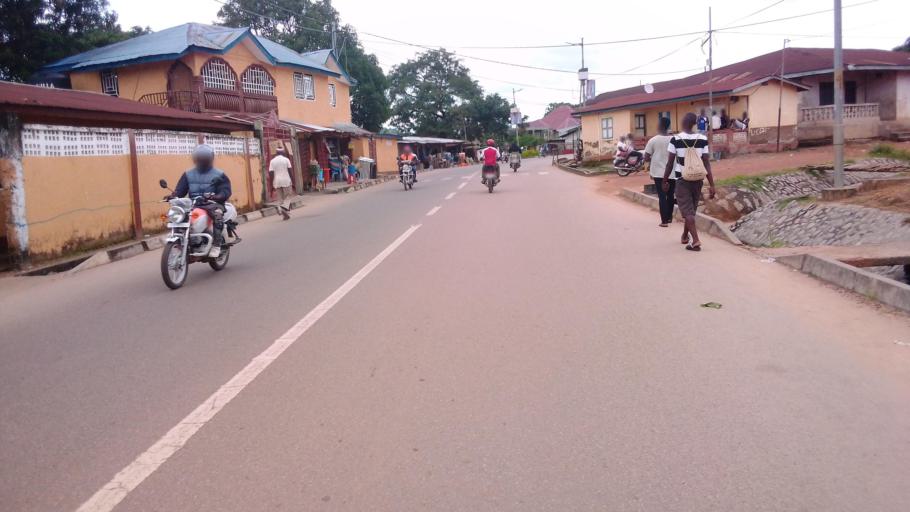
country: SL
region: Northern Province
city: Makeni
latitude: 8.8782
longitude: -12.0447
